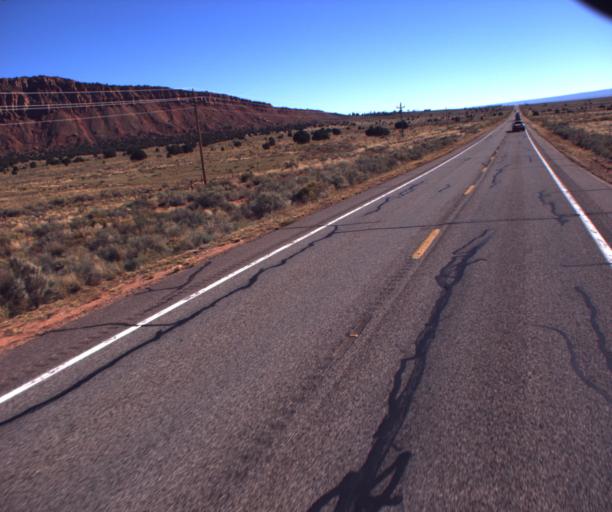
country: US
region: Arizona
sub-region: Mohave County
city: Colorado City
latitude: 36.8579
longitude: -112.7662
